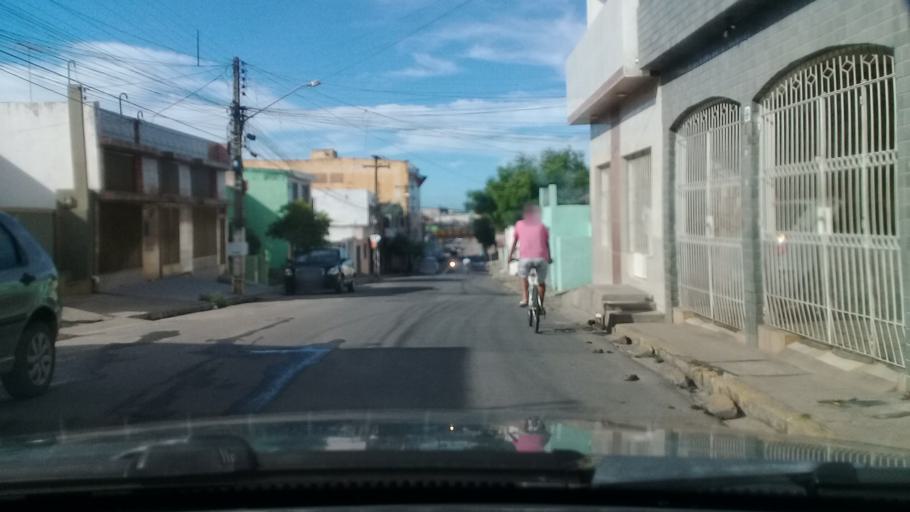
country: BR
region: Pernambuco
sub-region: Vitoria De Santo Antao
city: Vitoria de Santo Antao
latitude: -8.1133
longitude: -35.2912
